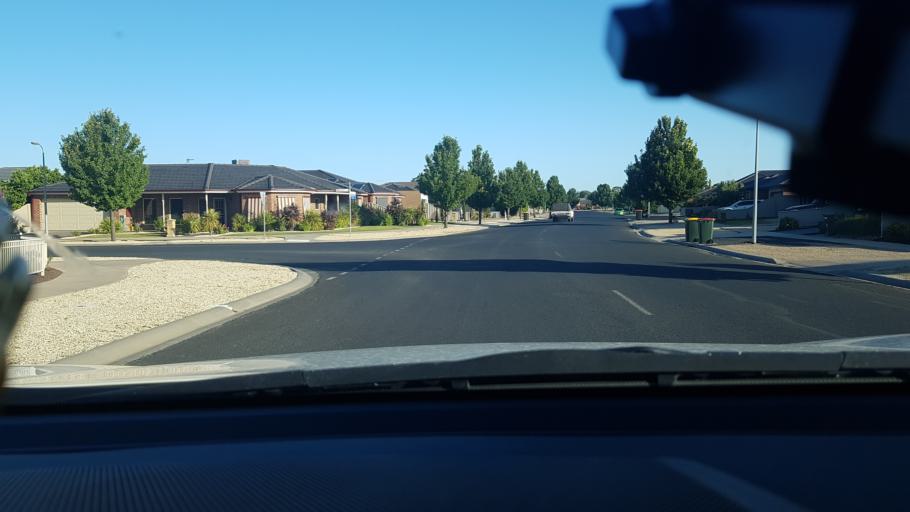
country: AU
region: Victoria
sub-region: Horsham
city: Horsham
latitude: -36.7122
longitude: 142.1790
